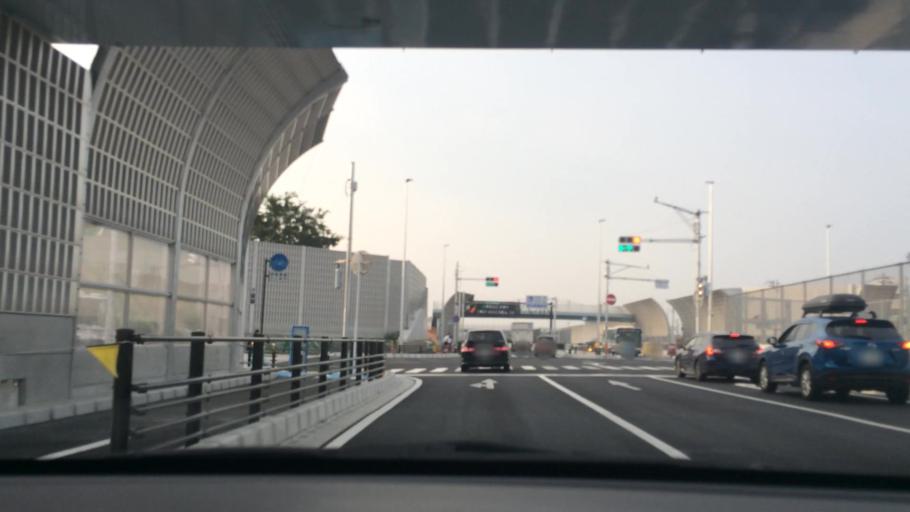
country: JP
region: Chiba
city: Matsudo
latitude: 35.7435
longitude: 139.9198
